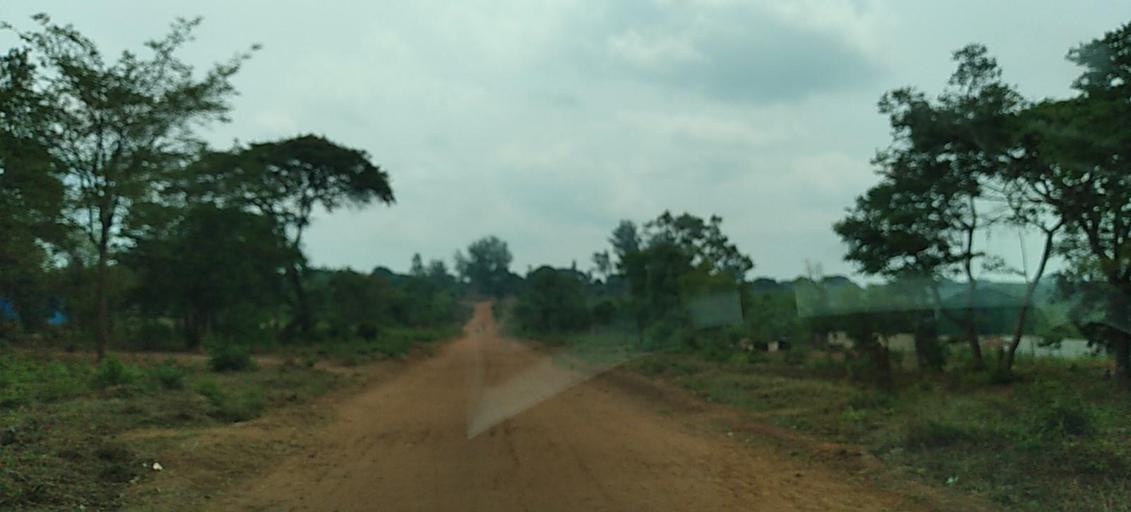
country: ZM
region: North-Western
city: Mwinilunga
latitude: -11.4450
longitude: 24.7482
